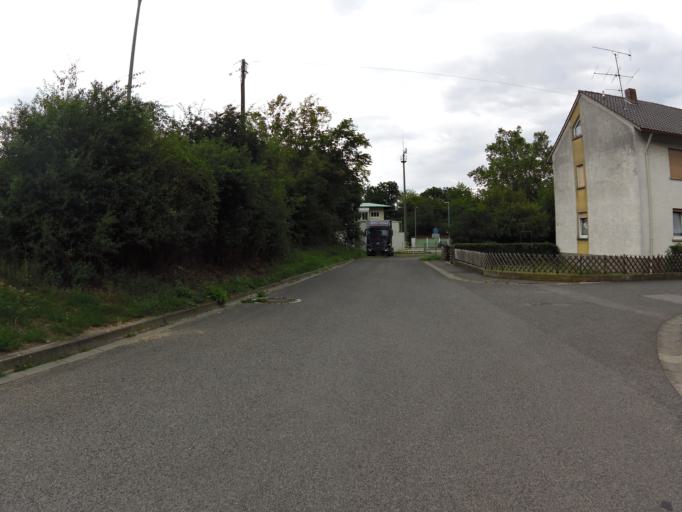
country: DE
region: Bavaria
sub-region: Regierungsbezirk Unterfranken
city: Eltmann
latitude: 49.9812
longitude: 10.6362
